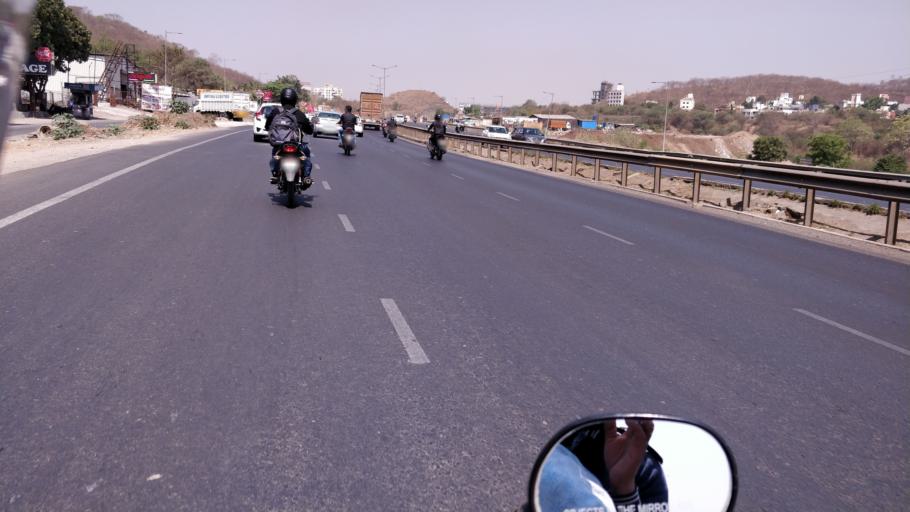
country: IN
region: Maharashtra
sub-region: Pune Division
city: Shivaji Nagar
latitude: 18.5418
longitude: 73.7778
